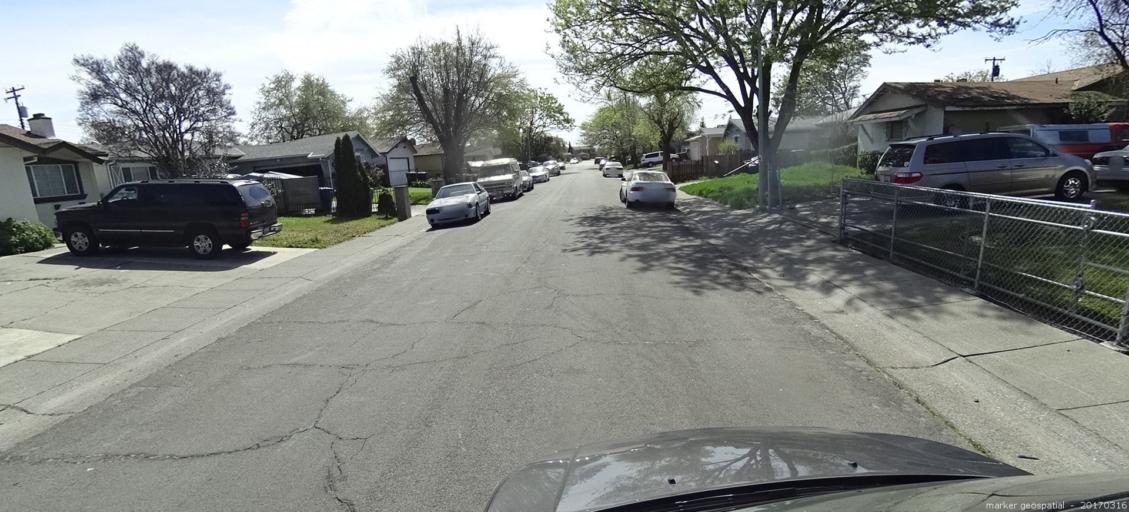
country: US
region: California
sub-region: Sacramento County
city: Parkway
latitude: 38.4800
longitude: -121.4879
